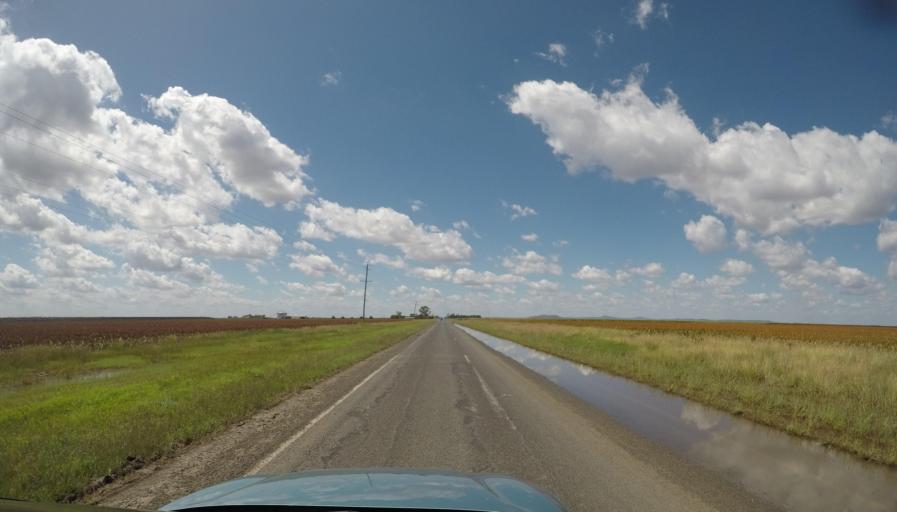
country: AU
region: Queensland
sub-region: Toowoomba
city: Oakey
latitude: -27.5179
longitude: 151.4125
